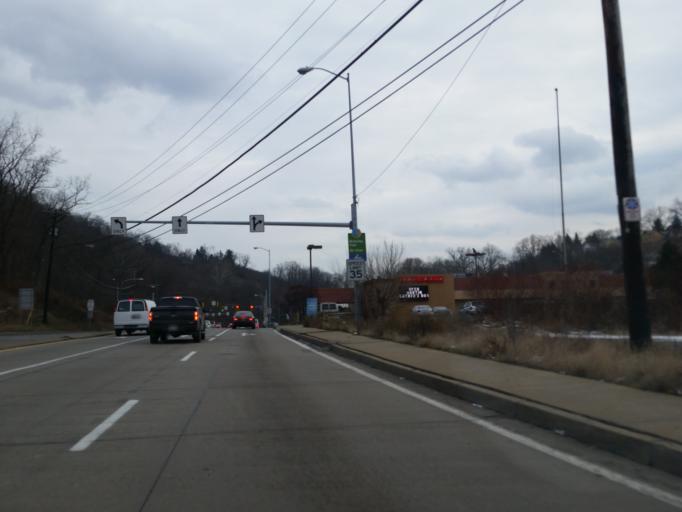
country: US
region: Pennsylvania
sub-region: Allegheny County
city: Mount Oliver
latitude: 40.4123
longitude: -80.0073
